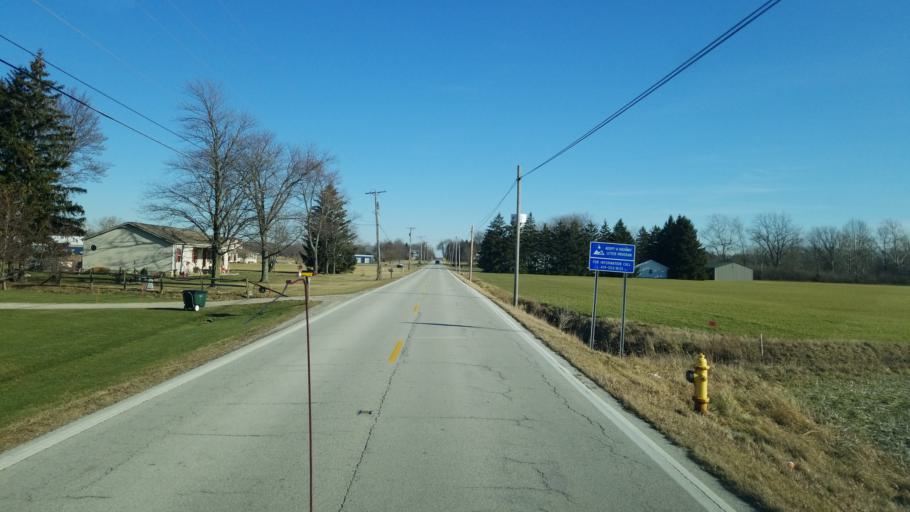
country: US
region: Ohio
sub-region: Wood County
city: Luckey
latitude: 41.4534
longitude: -83.4710
